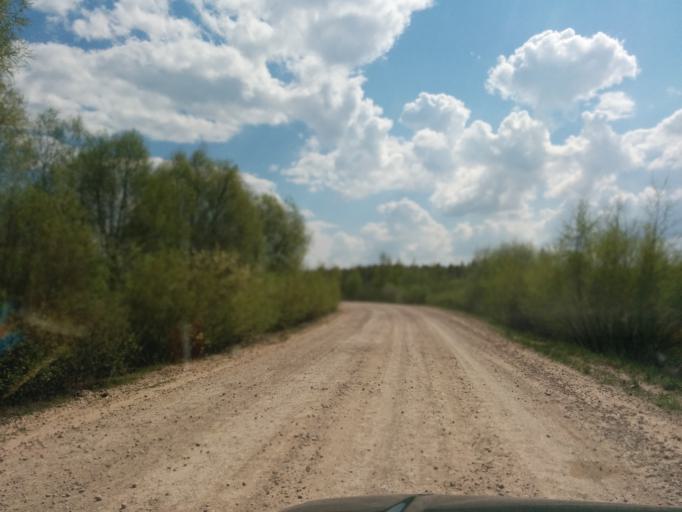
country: LV
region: Ozolnieku
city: Ozolnieki
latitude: 56.6373
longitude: 23.7910
